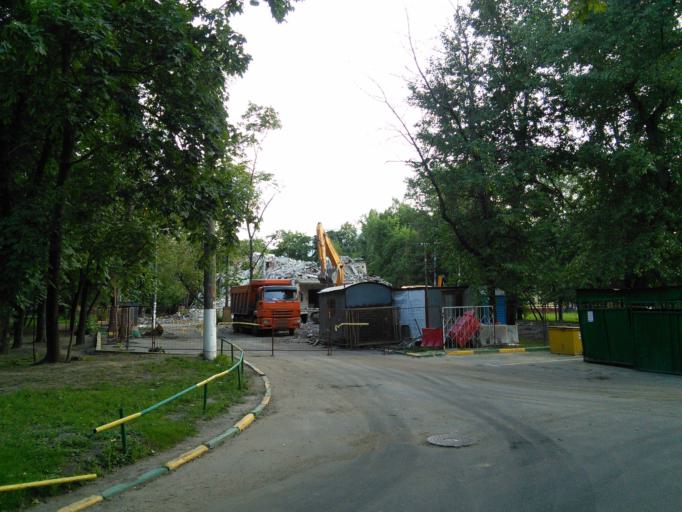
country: RU
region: Moscow
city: Novyye Kuz'minki
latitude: 55.7091
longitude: 37.7544
